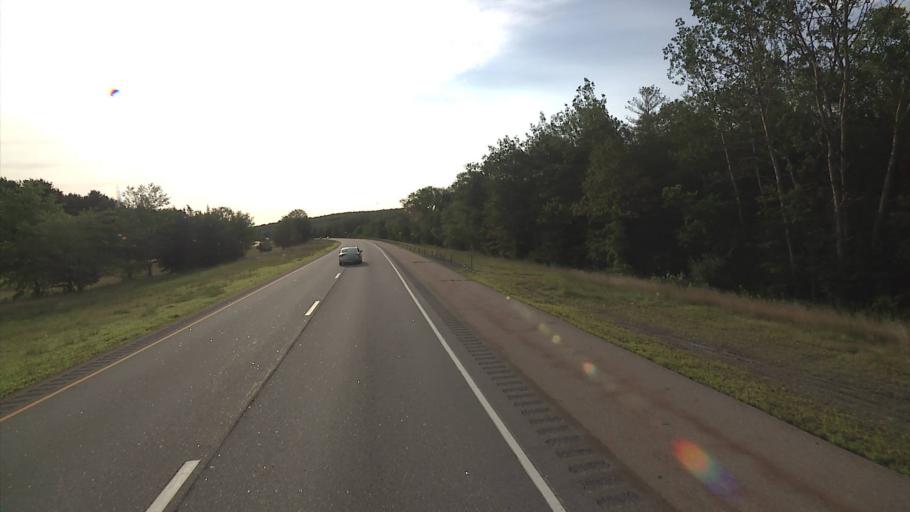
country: US
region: Connecticut
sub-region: New London County
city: Colchester
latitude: 41.5654
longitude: -72.2462
